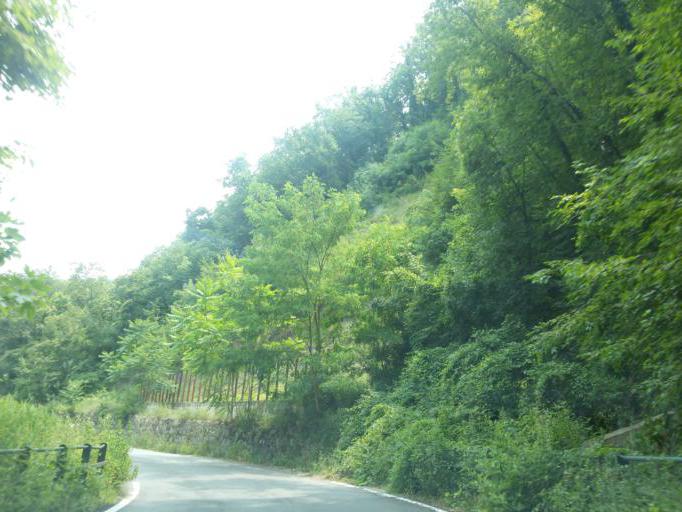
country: IT
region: Liguria
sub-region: Provincia di Genova
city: Piccarello
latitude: 44.4389
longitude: 9.0056
